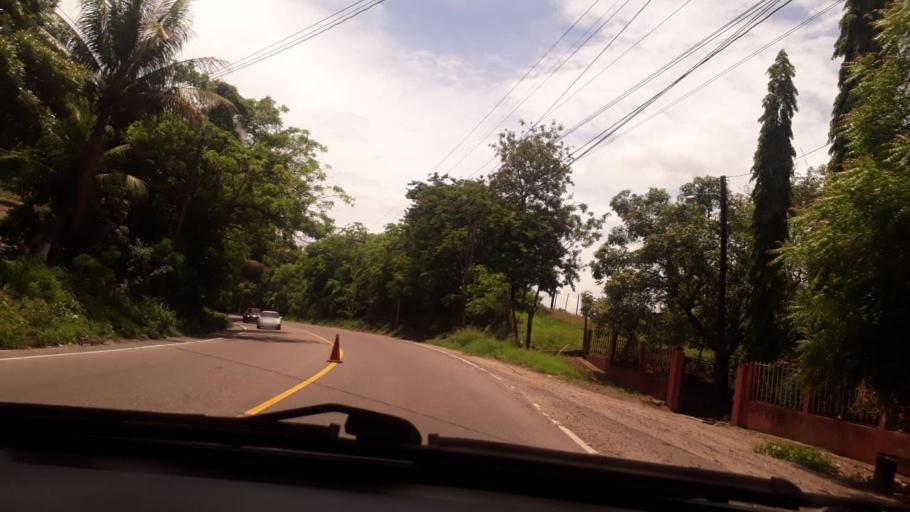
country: GT
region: Zacapa
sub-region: Municipio de Zacapa
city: Gualan
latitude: 15.1263
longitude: -89.3750
